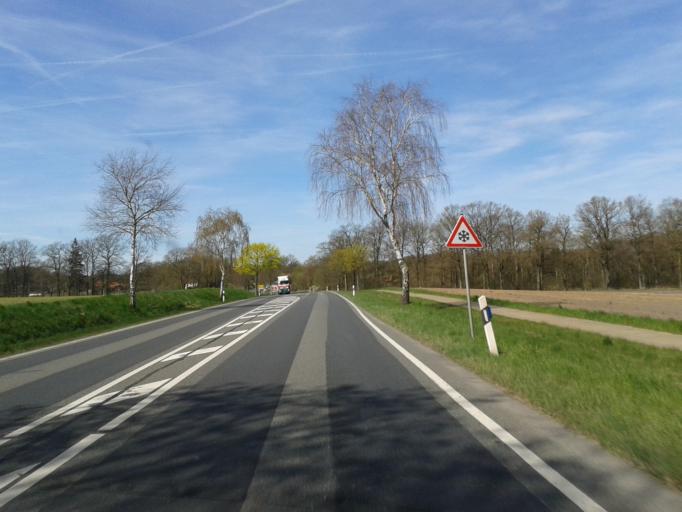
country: DE
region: Lower Saxony
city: Eimke
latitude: 52.9669
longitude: 10.3279
